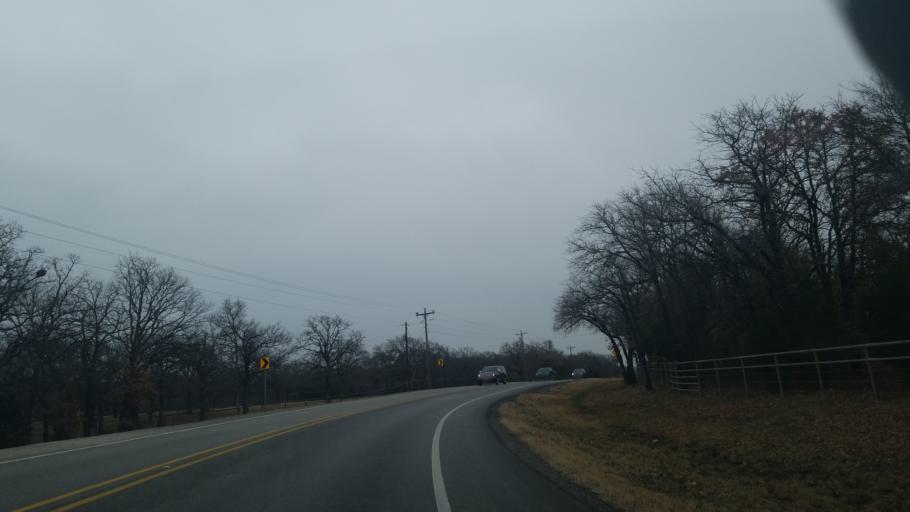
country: US
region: Texas
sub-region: Denton County
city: Argyle
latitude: 33.1322
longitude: -97.1459
